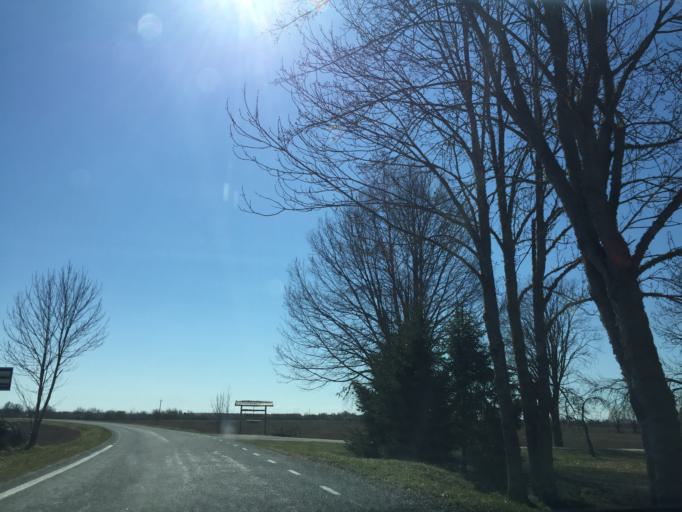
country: EE
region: Jogevamaa
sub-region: Poltsamaa linn
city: Poltsamaa
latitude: 58.3787
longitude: 25.9419
